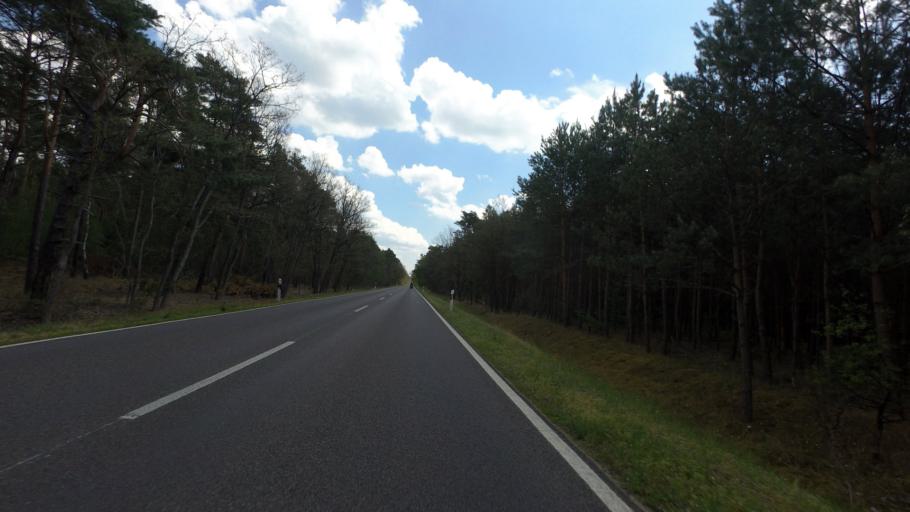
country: DE
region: Brandenburg
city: Neu Zauche
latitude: 51.9448
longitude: 14.0170
